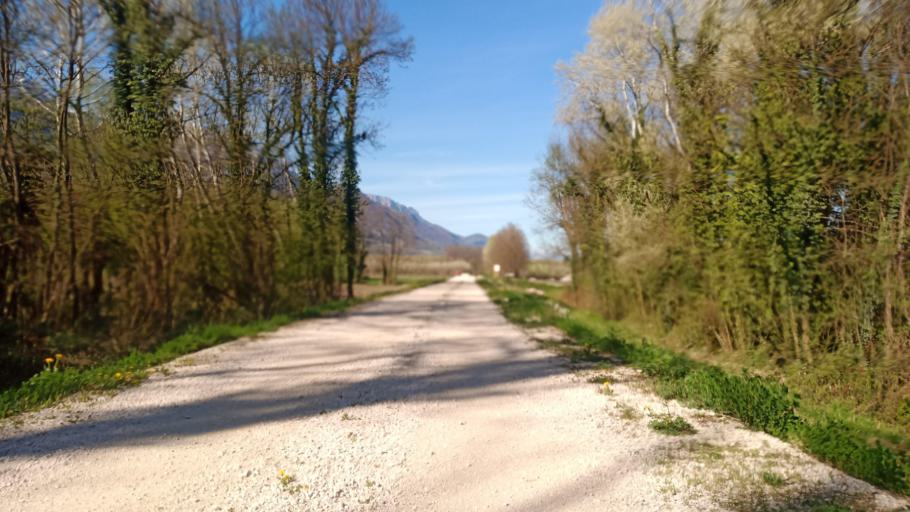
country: FR
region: Rhone-Alpes
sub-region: Departement de l'Isere
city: Froges
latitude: 45.2826
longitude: 5.9203
